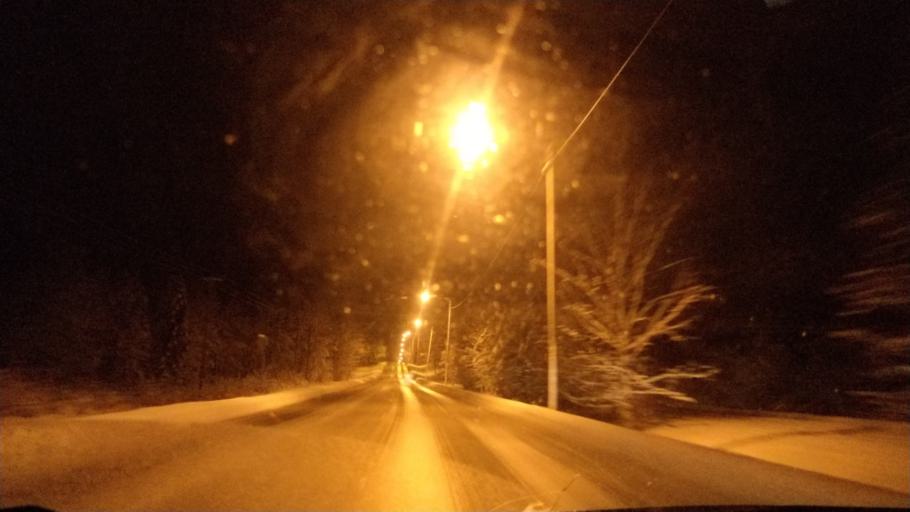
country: FI
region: Lapland
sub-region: Rovaniemi
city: Rovaniemi
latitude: 66.3012
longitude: 25.3539
